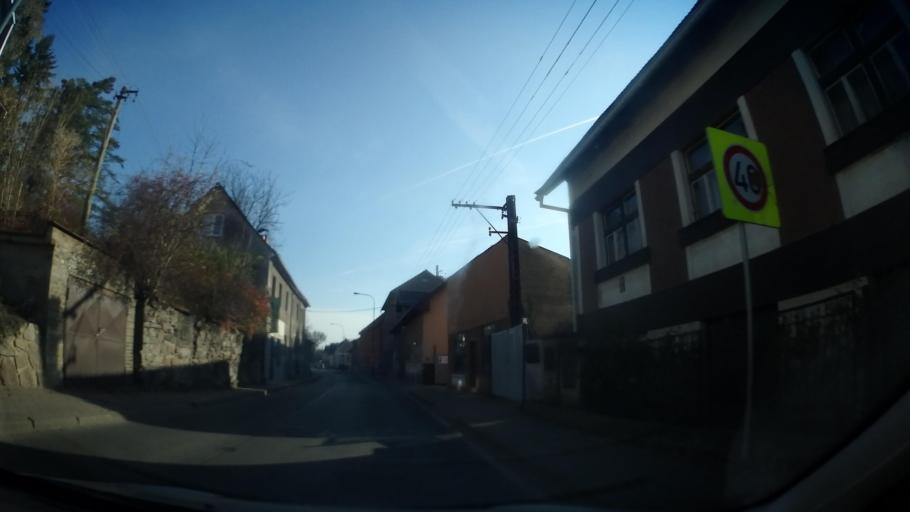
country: CZ
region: Central Bohemia
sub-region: Okres Praha-Vychod
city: Mnichovice
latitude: 49.9351
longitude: 14.7106
